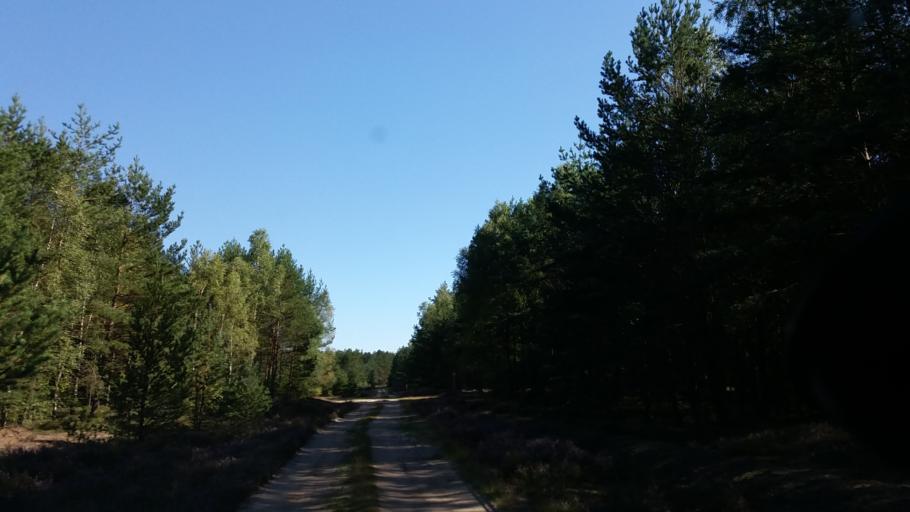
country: PL
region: West Pomeranian Voivodeship
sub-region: Powiat szczecinecki
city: Borne Sulinowo
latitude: 53.5650
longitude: 16.5000
